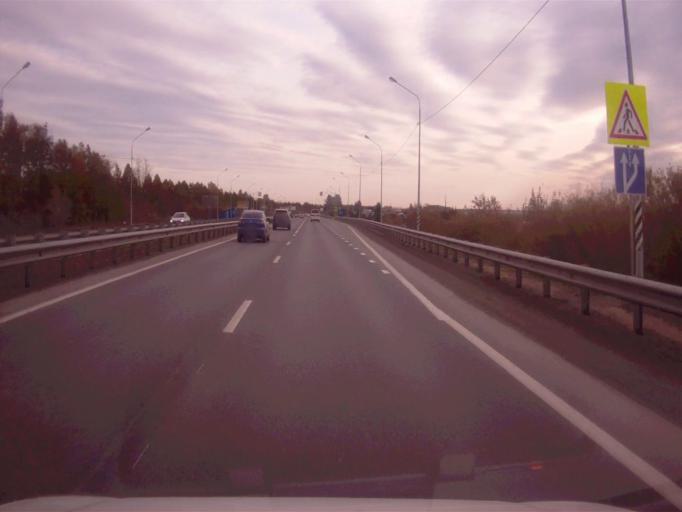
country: RU
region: Chelyabinsk
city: Novosineglazovskiy
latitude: 55.0327
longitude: 61.4441
